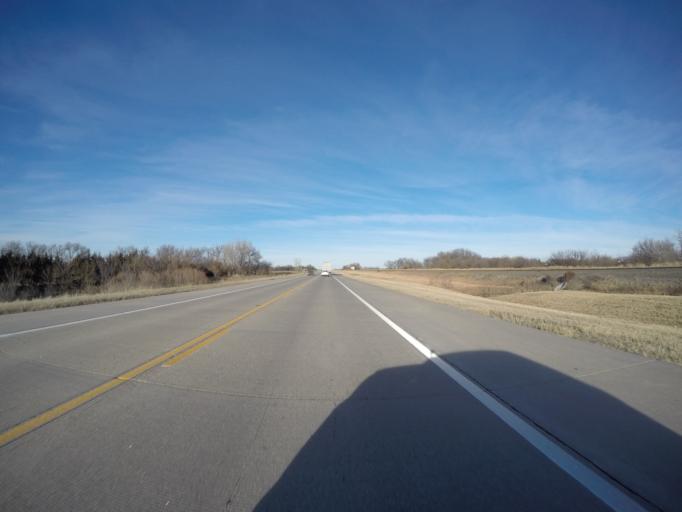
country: US
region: Kansas
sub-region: Harvey County
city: North Newton
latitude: 38.0777
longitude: -97.2967
